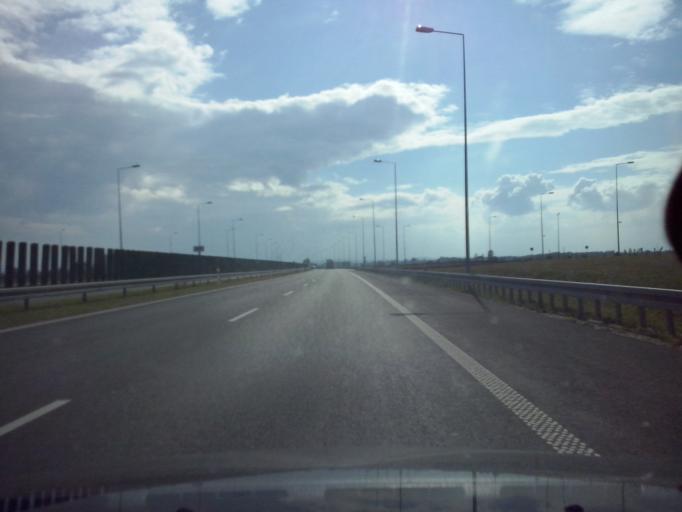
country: PL
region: Lesser Poland Voivodeship
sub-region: Powiat tarnowski
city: Wierzchoslawice
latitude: 50.0413
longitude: 20.8890
